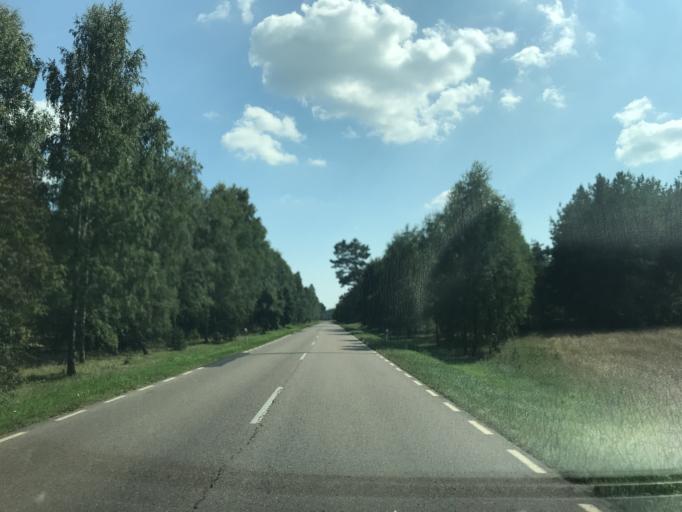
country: PL
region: Warmian-Masurian Voivodeship
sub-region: Powiat dzialdowski
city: Lidzbark
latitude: 53.1999
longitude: 19.8450
